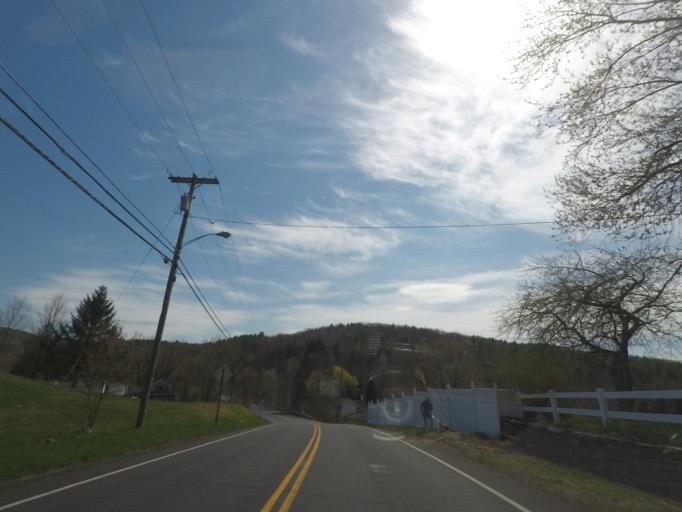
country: US
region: New York
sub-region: Columbia County
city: Chatham
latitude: 42.4089
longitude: -73.5262
